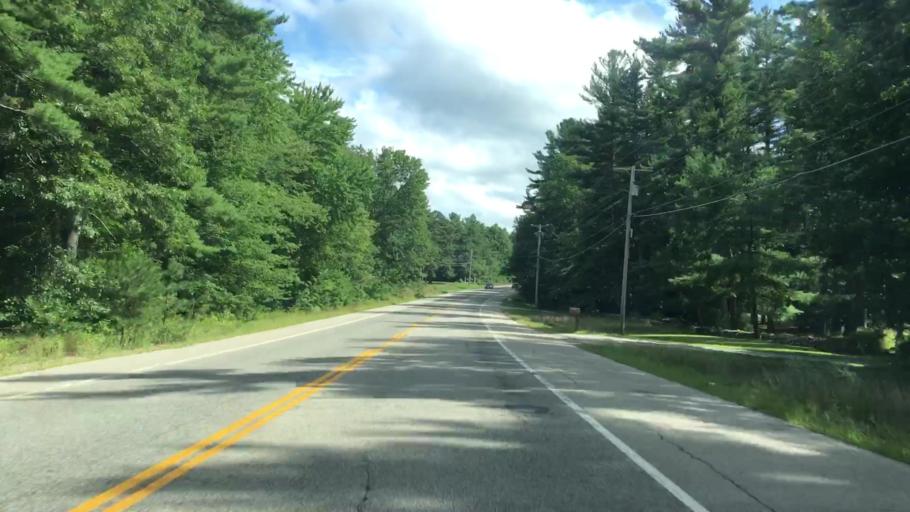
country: US
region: Maine
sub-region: York County
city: South Sanford
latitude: 43.3739
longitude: -70.7373
